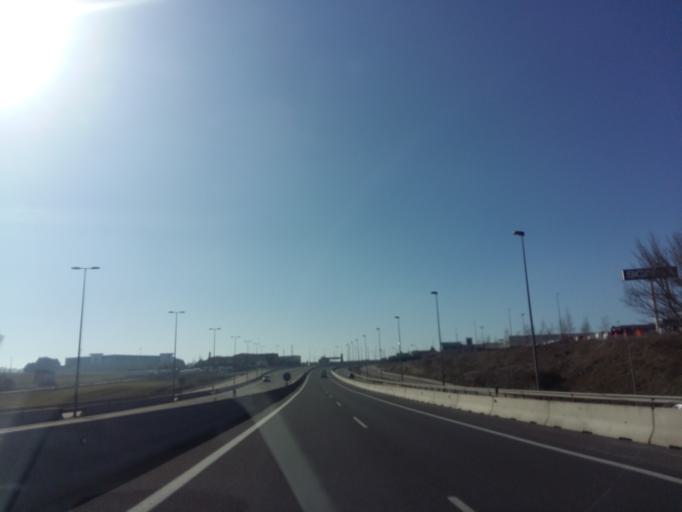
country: ES
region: Castille and Leon
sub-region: Provincia de Burgos
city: Villagonzalo-Pedernales
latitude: 42.2947
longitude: -3.7034
